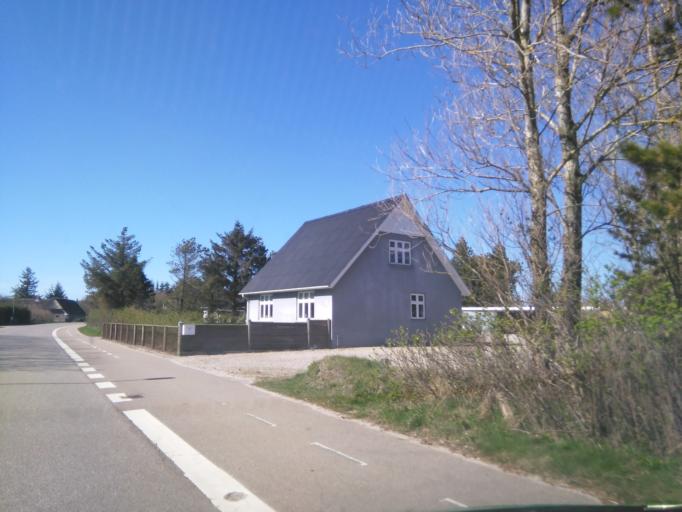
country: DK
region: South Denmark
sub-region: Varde Kommune
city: Oksbol
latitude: 55.5515
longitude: 8.1452
